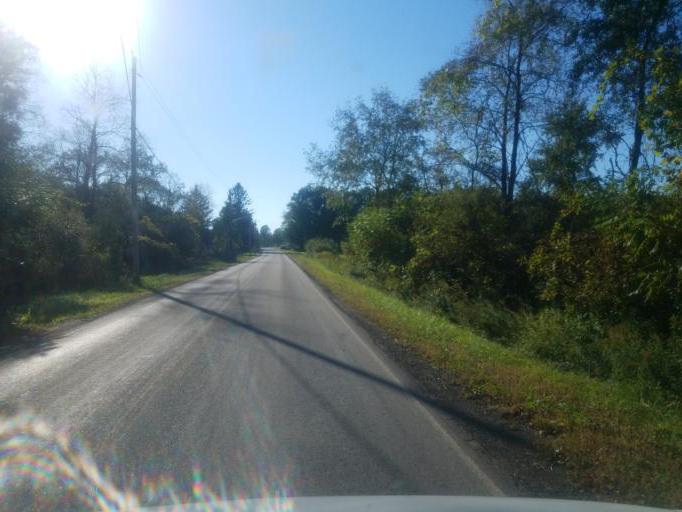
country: US
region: New York
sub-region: Allegany County
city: Cuba
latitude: 42.2758
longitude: -78.2217
